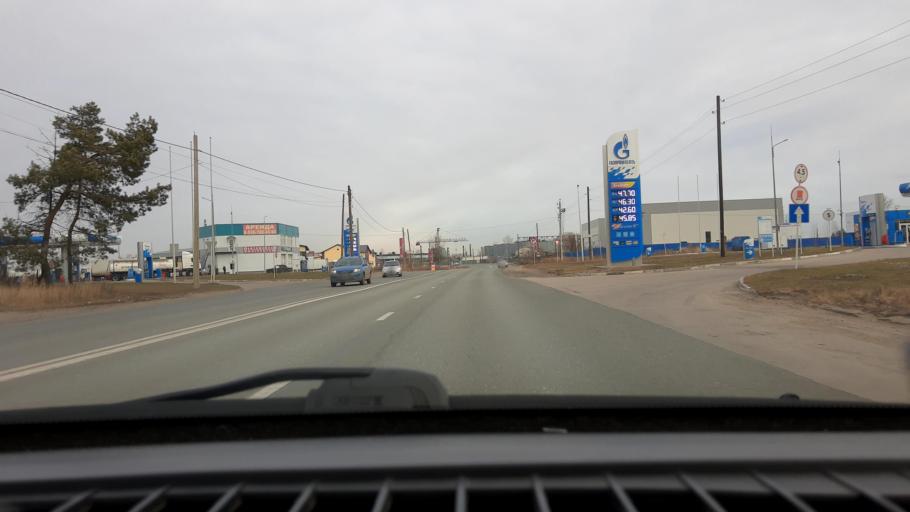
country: RU
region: Nizjnij Novgorod
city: Gorbatovka
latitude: 56.3330
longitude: 43.7932
